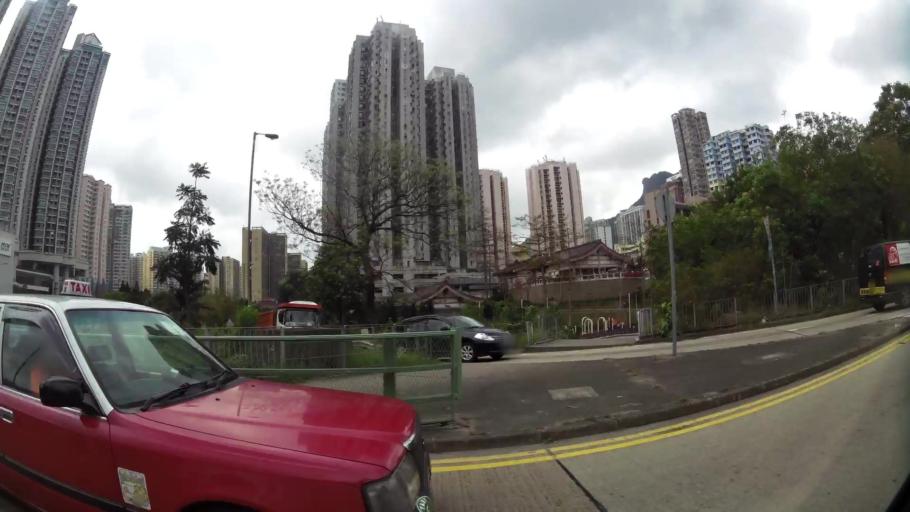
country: HK
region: Wong Tai Sin
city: Wong Tai Sin
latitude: 22.3420
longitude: 114.1985
